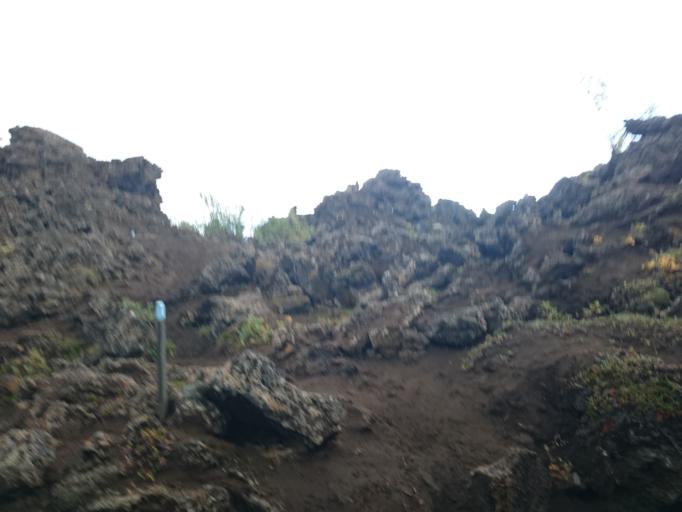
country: IS
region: Northeast
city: Laugar
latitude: 65.5887
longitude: -16.9115
